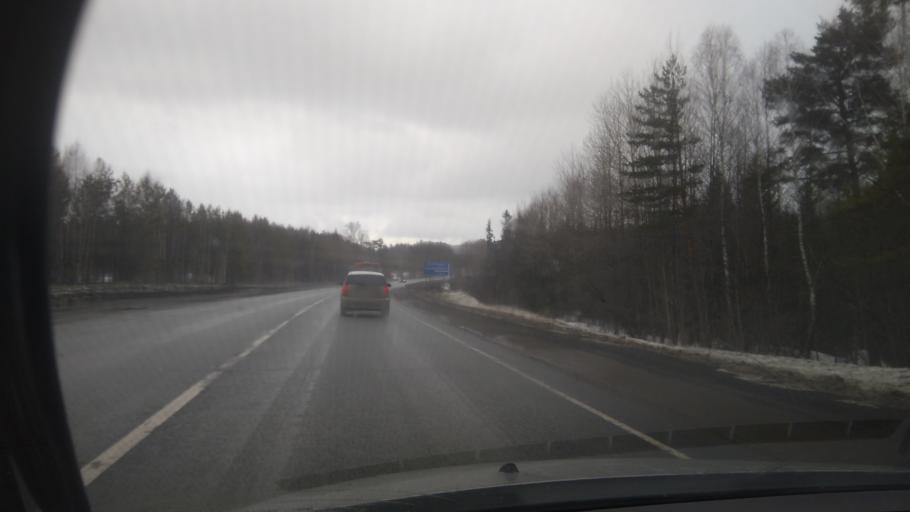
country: RU
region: Sverdlovsk
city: Ufimskiy
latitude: 56.7804
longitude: 58.2611
